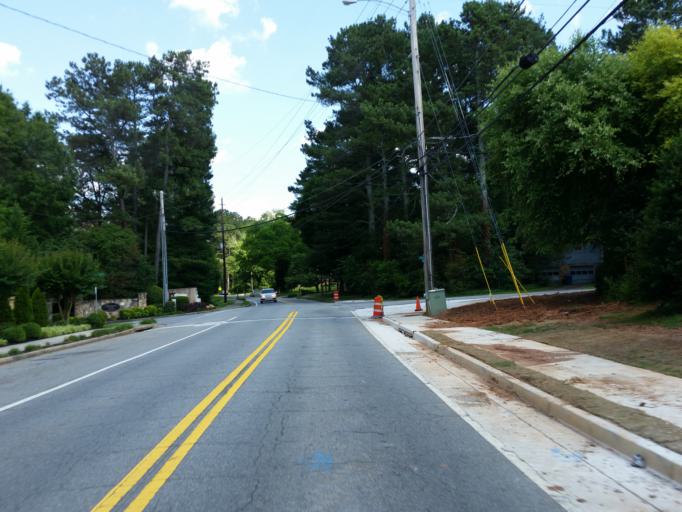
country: US
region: Georgia
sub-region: Cherokee County
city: Woodstock
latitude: 34.0293
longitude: -84.4945
